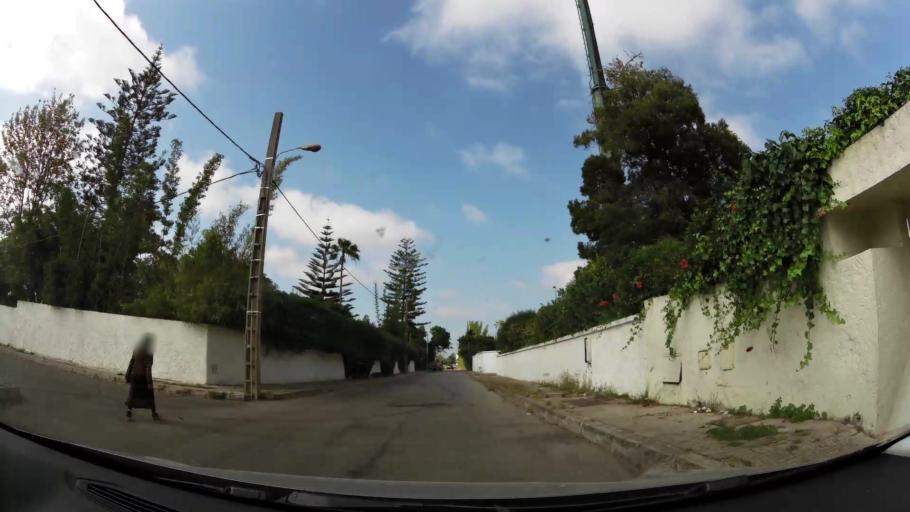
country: MA
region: Rabat-Sale-Zemmour-Zaer
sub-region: Rabat
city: Rabat
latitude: 33.9679
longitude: -6.8512
